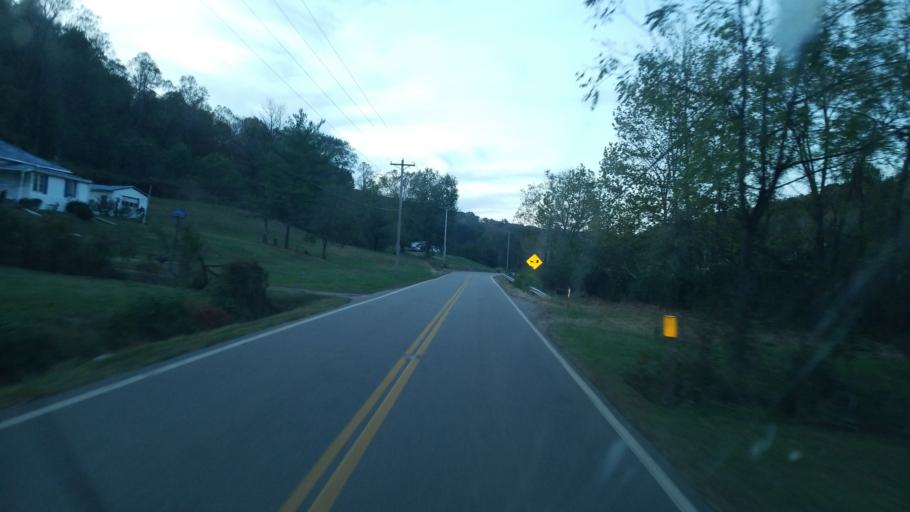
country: US
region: Ohio
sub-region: Meigs County
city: Pomeroy
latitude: 39.0403
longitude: -82.0623
